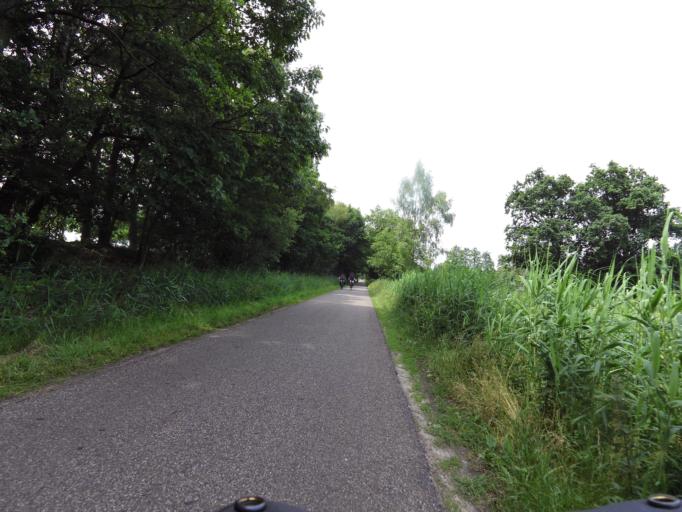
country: NL
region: Gelderland
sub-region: Gemeente Apeldoorn
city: Loenen
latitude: 52.1582
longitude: 6.0156
